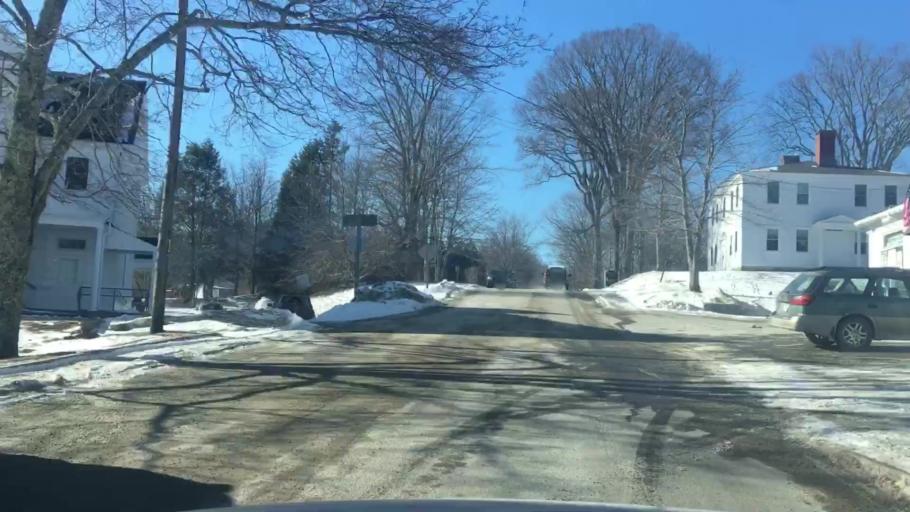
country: US
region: Maine
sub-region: Hancock County
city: Sedgwick
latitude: 44.4131
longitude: -68.5889
